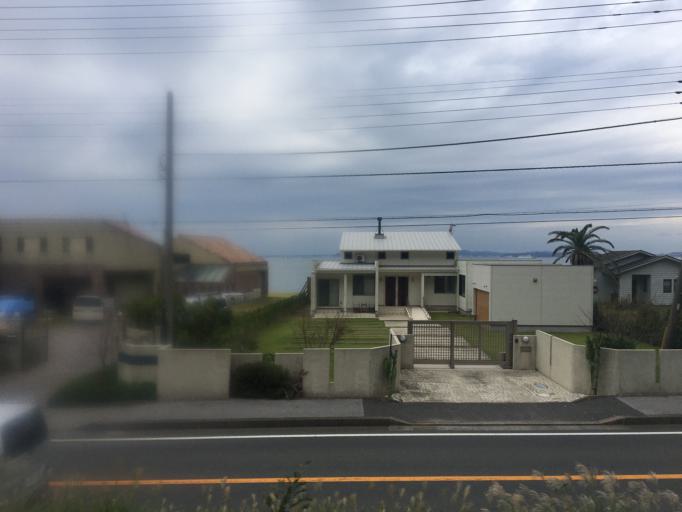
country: JP
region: Chiba
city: Futtsu
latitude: 35.1882
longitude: 139.8197
